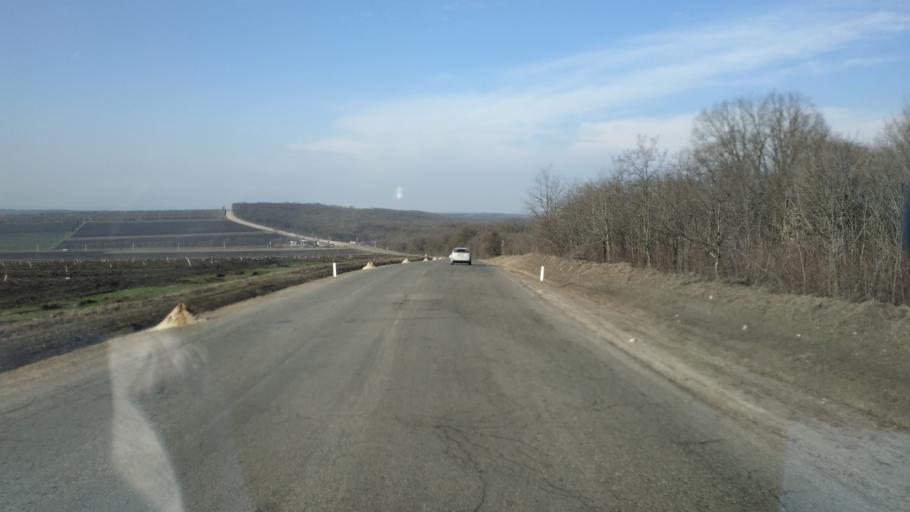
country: MD
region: Chisinau
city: Singera
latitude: 46.8578
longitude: 29.0304
